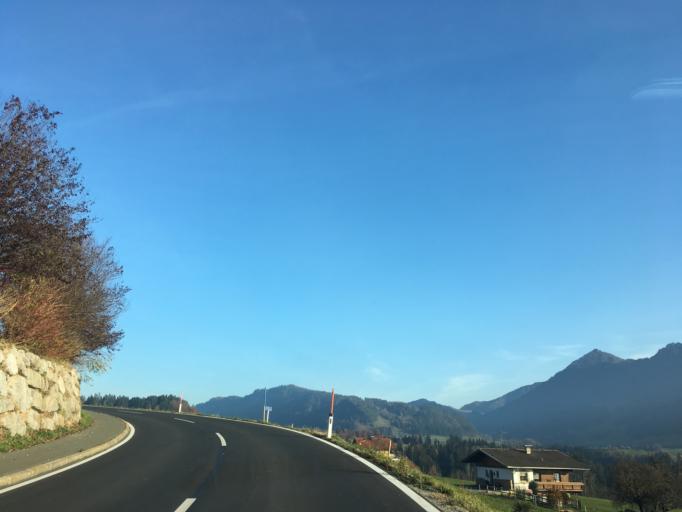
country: AT
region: Tyrol
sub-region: Politischer Bezirk Kufstein
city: Niederndorf
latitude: 47.6523
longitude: 12.2416
